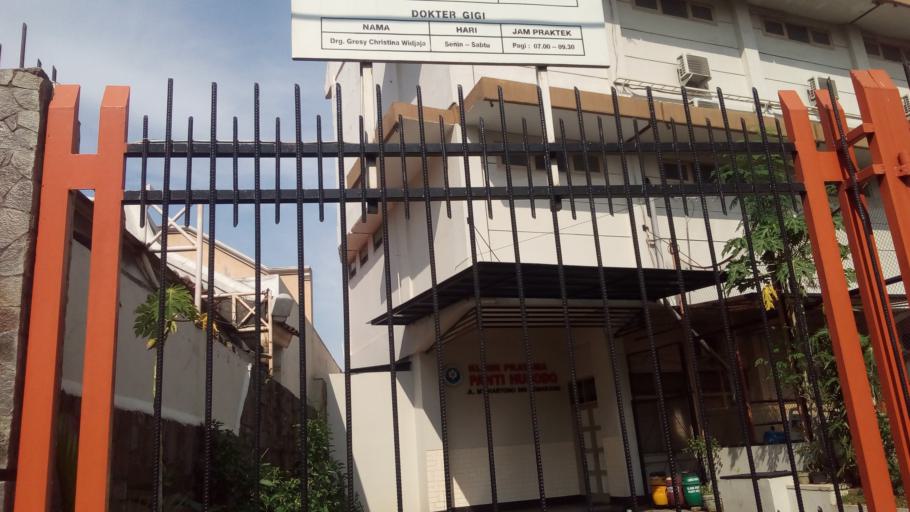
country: ID
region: Central Java
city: Semarang
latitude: -6.9987
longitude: 110.4323
